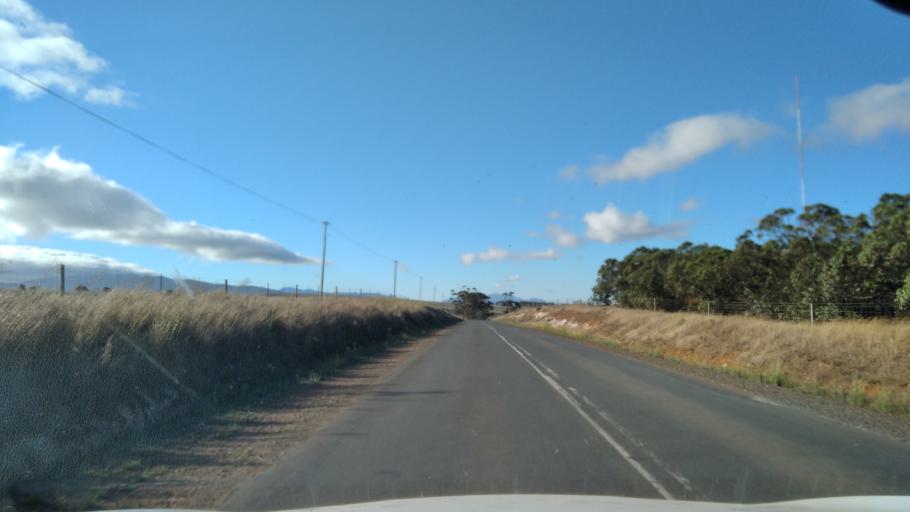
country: ZA
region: Western Cape
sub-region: Overberg District Municipality
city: Caledon
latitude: -34.2164
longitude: 19.2758
